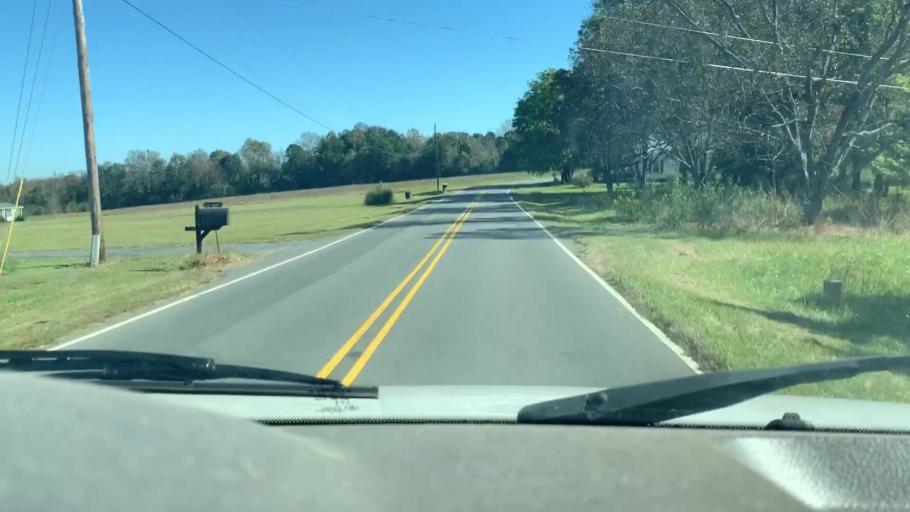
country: US
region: North Carolina
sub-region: Mecklenburg County
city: Cornelius
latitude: 35.4544
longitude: -80.8357
